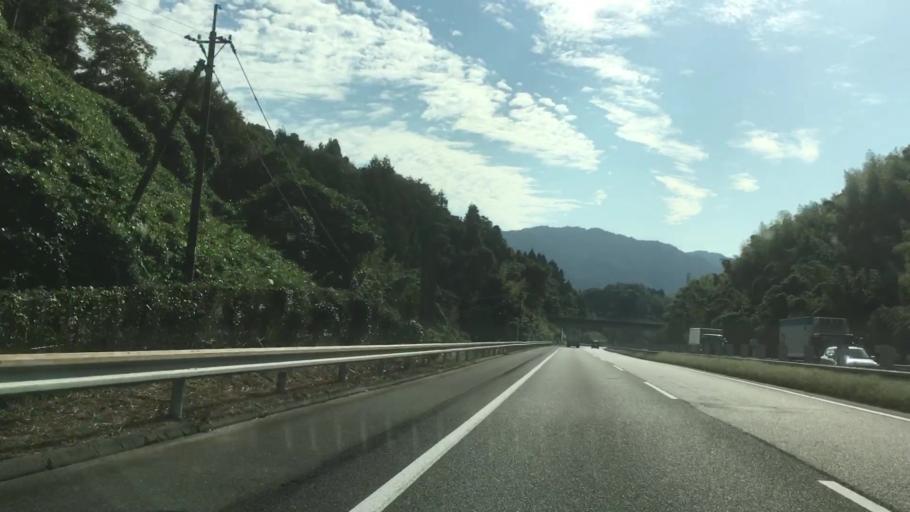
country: JP
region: Yamaguchi
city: Hikari
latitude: 34.0316
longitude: 131.9665
